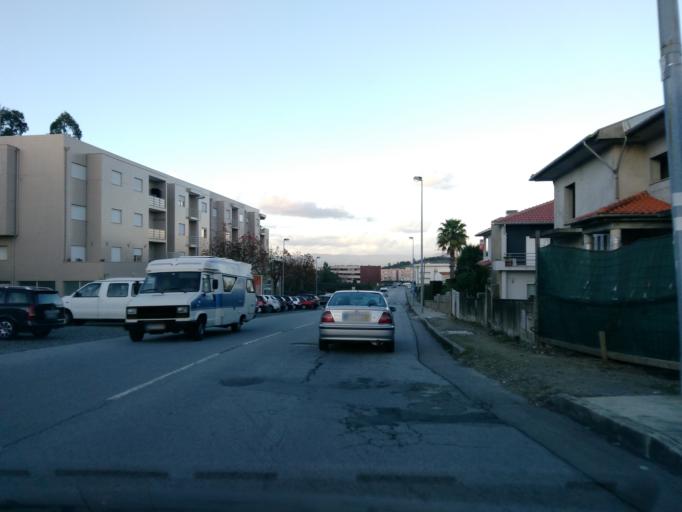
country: PT
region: Braga
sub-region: Braga
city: Braga
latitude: 41.5305
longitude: -8.4549
